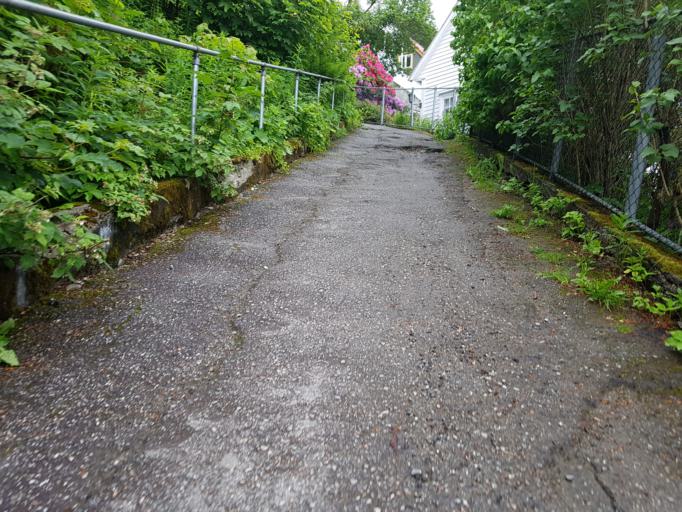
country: NO
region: Hordaland
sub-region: Bergen
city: Bergen
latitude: 60.3951
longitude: 5.3368
